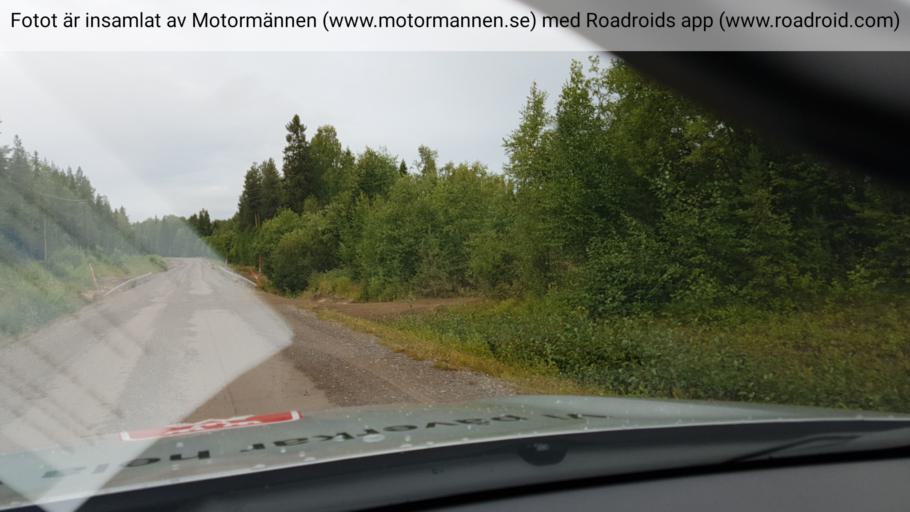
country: SE
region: Norrbotten
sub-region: Alvsbyns Kommun
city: AElvsbyn
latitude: 66.0103
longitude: 21.0927
